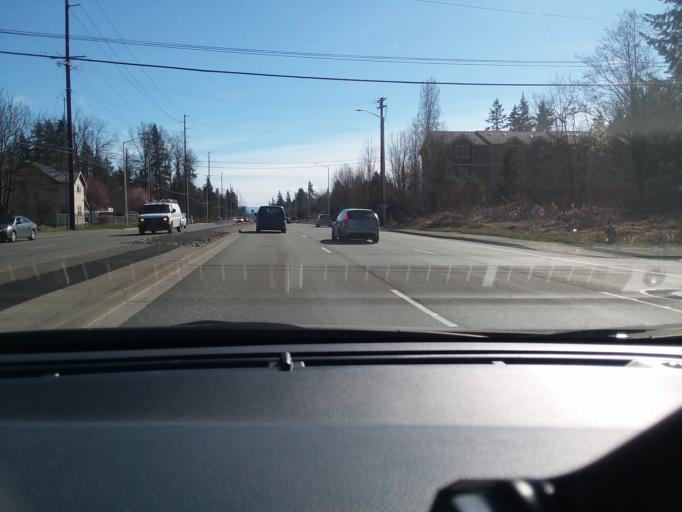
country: US
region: Washington
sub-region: Pierce County
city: Frederickson
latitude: 47.1232
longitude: -122.3576
